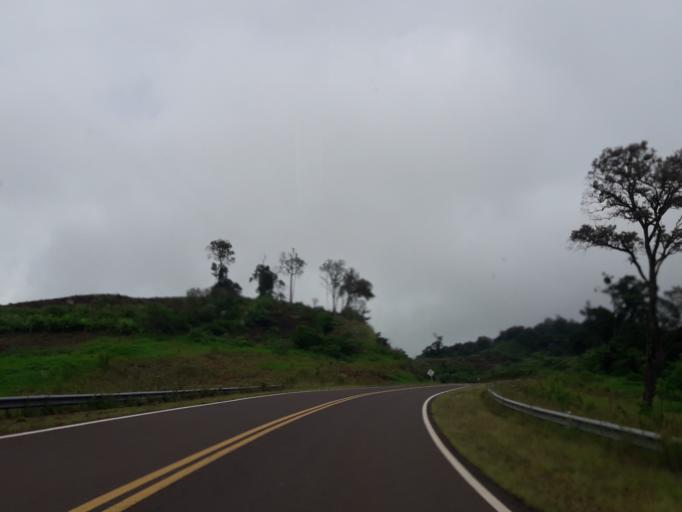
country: AR
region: Misiones
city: Bernardo de Irigoyen
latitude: -26.3990
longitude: -53.8168
